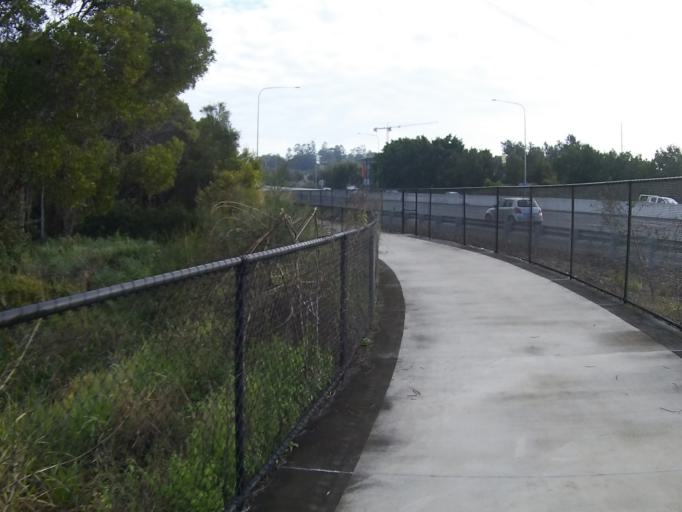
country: AU
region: Queensland
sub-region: Brisbane
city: Upper Mount Gravatt
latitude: -27.5801
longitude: 153.1020
